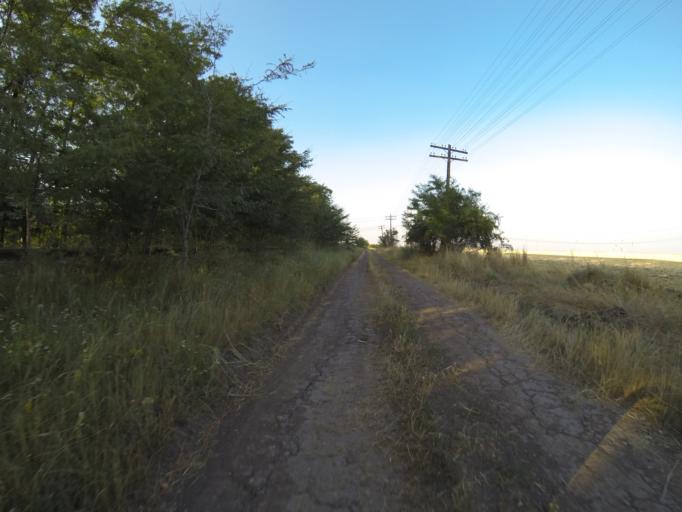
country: RO
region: Dolj
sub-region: Comuna Ceratu
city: Ceratu
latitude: 44.0431
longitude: 23.6549
